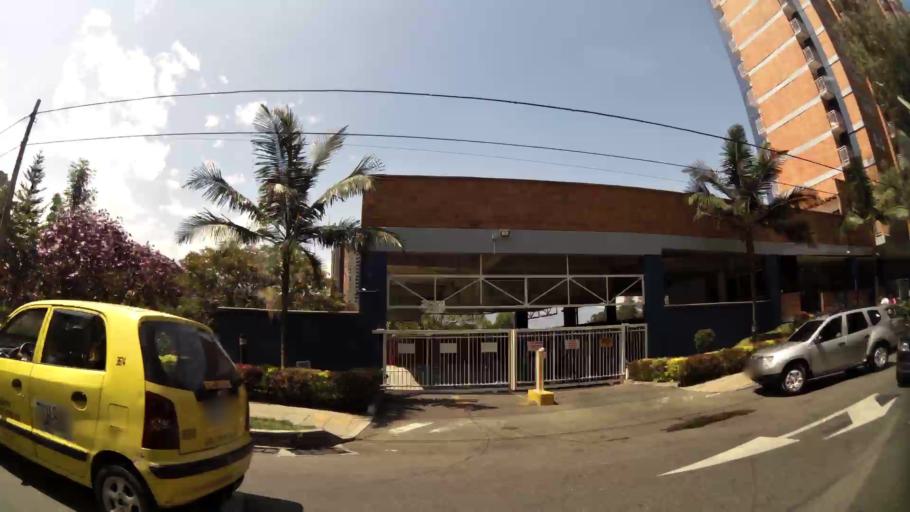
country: CO
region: Antioquia
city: Itagui
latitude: 6.2028
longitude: -75.5997
